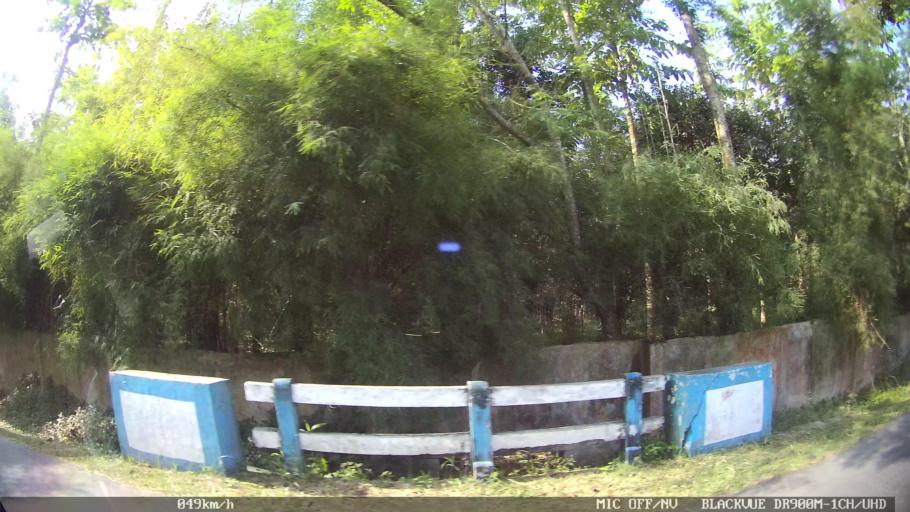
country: ID
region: North Sumatra
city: Percut
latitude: 3.5933
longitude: 98.8044
